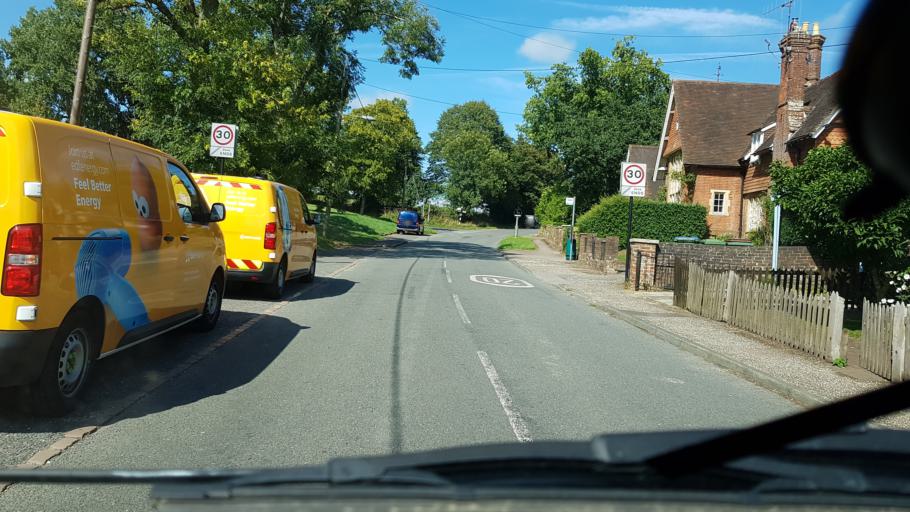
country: GB
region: England
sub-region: West Sussex
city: Horsham
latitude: 51.0922
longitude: -0.3462
